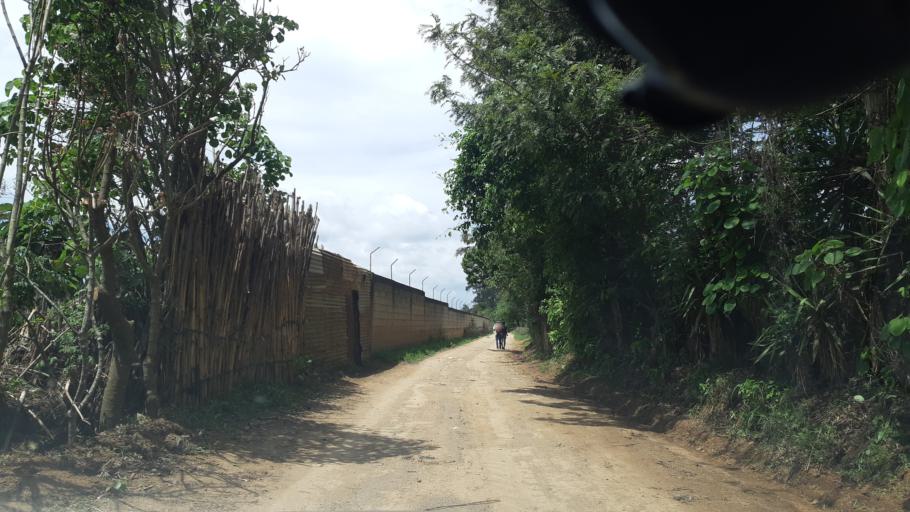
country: GT
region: Chimaltenango
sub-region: Municipio de Chimaltenango
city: Chimaltenango
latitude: 14.6546
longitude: -90.8425
